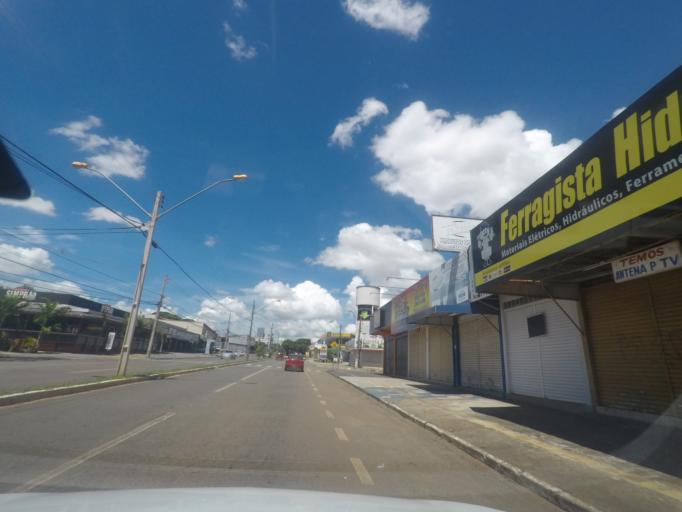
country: BR
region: Goias
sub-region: Goiania
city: Goiania
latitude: -16.6881
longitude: -49.2978
